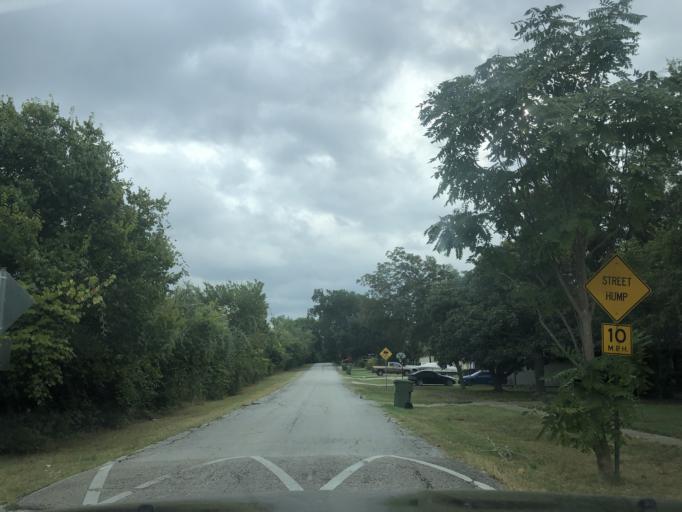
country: US
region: Texas
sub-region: Dallas County
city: Garland
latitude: 32.8891
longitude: -96.6475
